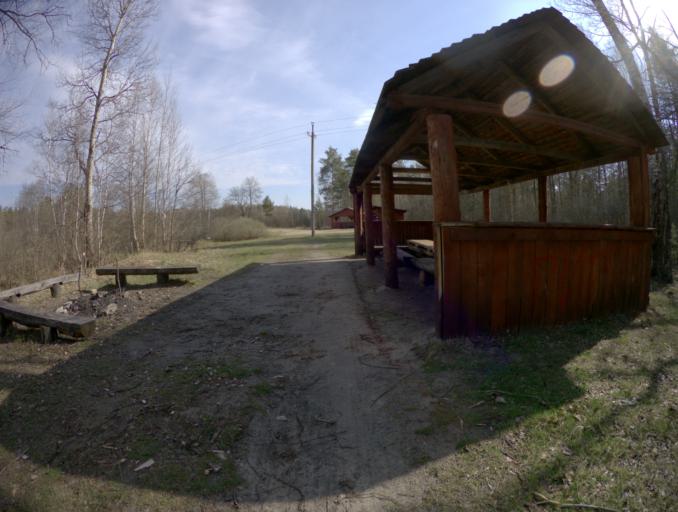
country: RU
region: Vladimir
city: Mezinovskiy
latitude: 55.5968
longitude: 40.3870
